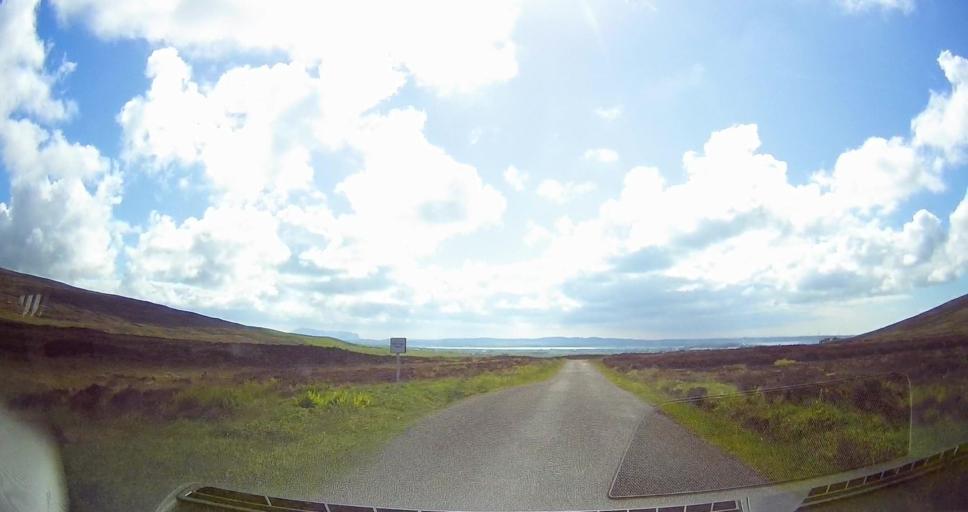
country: GB
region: Scotland
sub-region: Orkney Islands
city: Orkney
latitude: 59.0477
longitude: -3.1304
